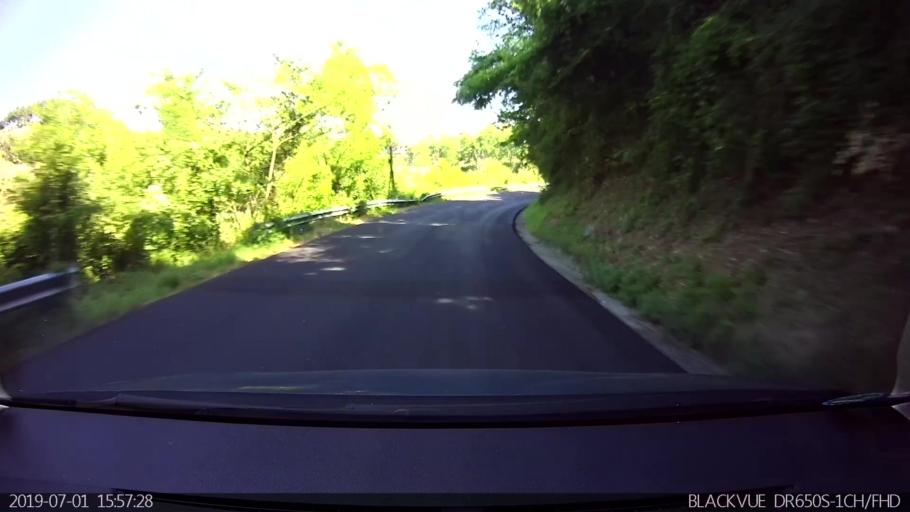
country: IT
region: Latium
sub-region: Provincia di Frosinone
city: Sant'Angelo in Villa-Giglio
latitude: 41.6759
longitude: 13.4219
